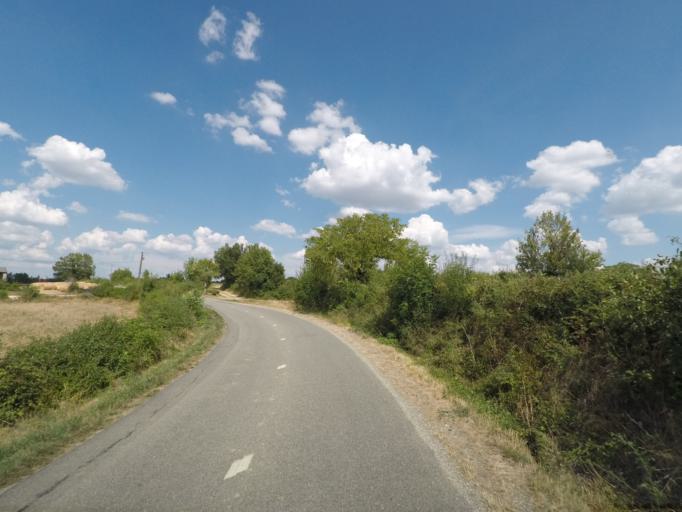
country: FR
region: Midi-Pyrenees
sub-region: Departement du Lot
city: Le Vigan
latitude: 44.6167
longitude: 1.5980
